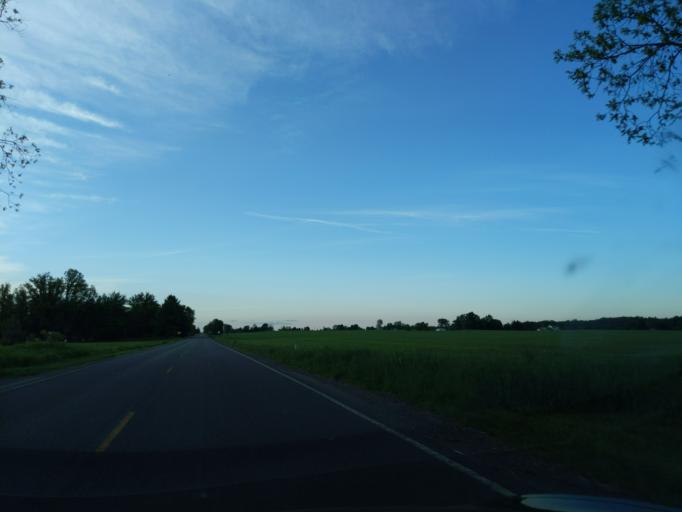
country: US
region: Michigan
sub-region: Ingham County
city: Williamston
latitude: 42.5720
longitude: -84.2984
